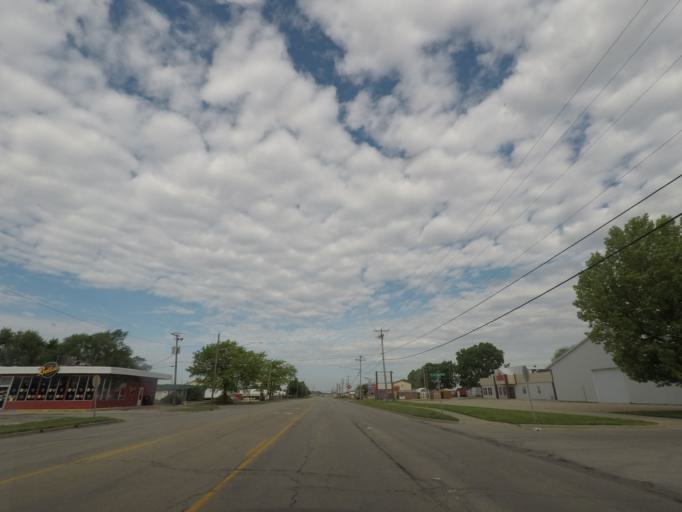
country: US
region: Illinois
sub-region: Logan County
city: Lincoln
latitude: 40.1577
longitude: -89.3809
